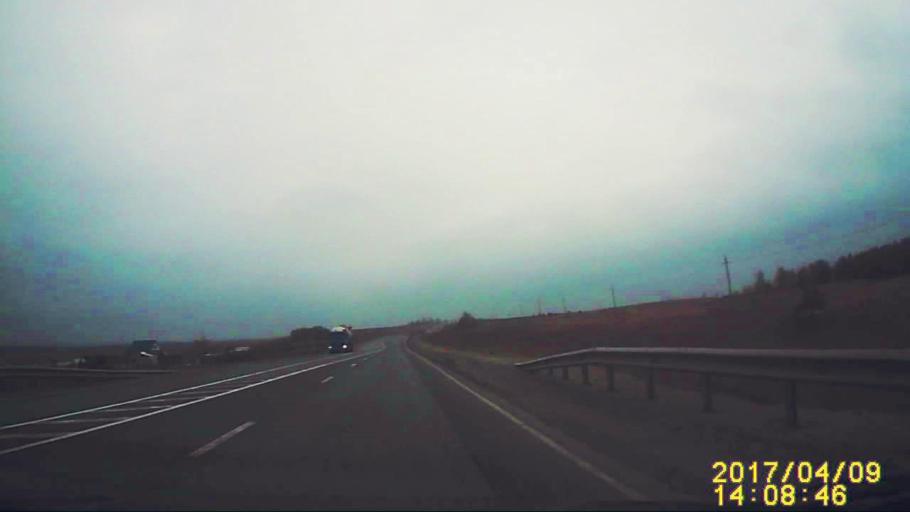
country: RU
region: Ulyanovsk
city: Silikatnyy
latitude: 54.0228
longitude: 48.2146
